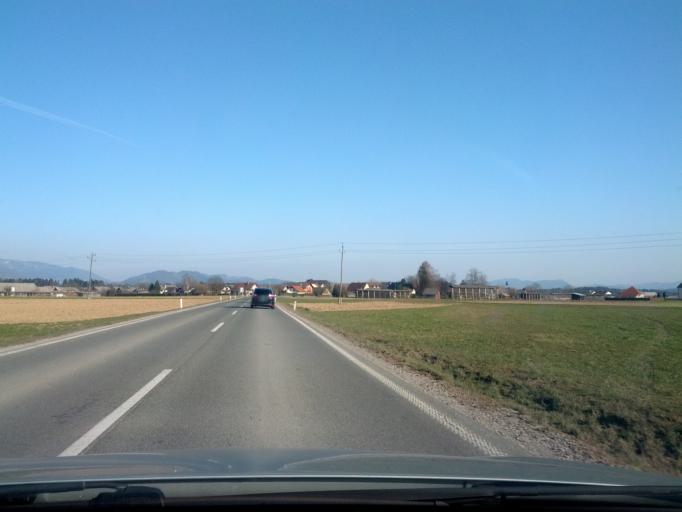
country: SI
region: Cerklje na Gorenjskem
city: Cerklje na Gorenjskem
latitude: 46.2308
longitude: 14.4776
